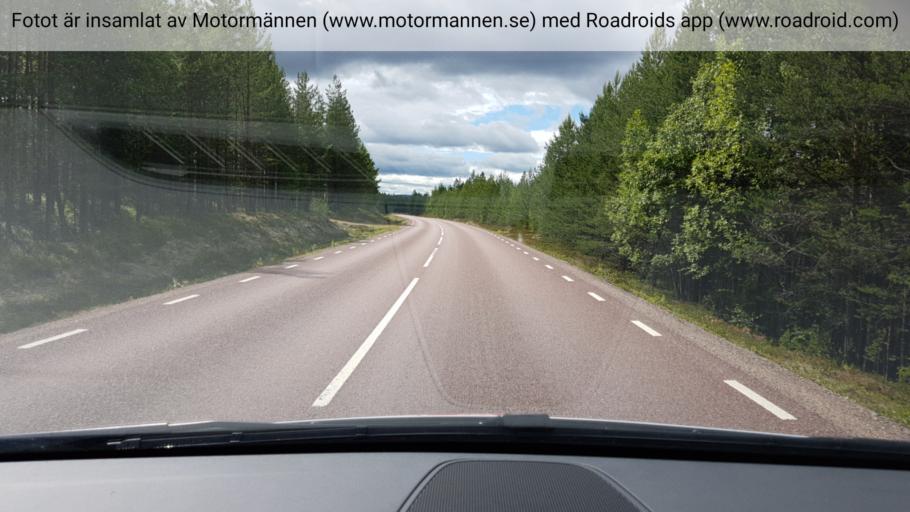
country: SE
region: Jaemtland
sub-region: Harjedalens Kommun
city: Sveg
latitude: 62.0077
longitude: 14.3034
